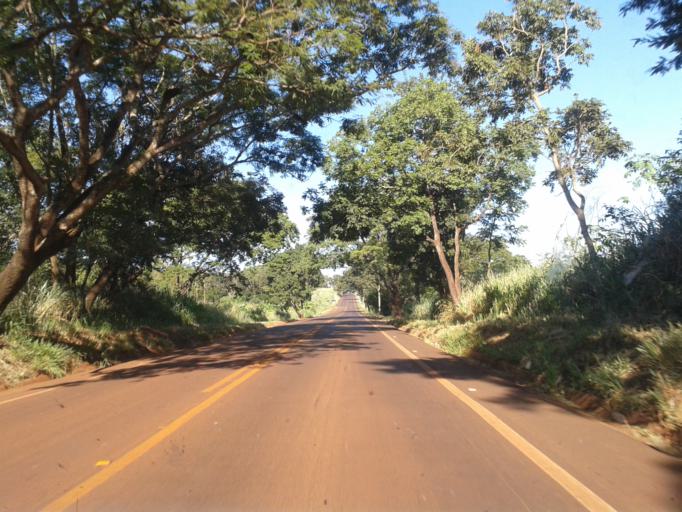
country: BR
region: Minas Gerais
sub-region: Capinopolis
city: Capinopolis
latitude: -18.6905
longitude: -49.6152
